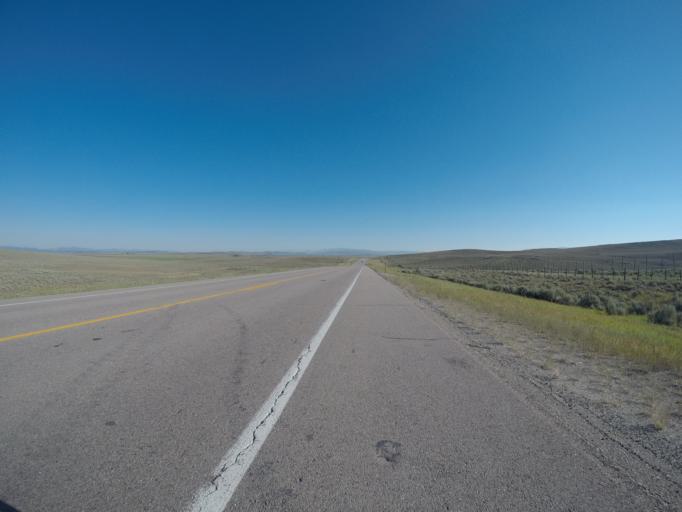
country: US
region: Wyoming
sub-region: Sublette County
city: Pinedale
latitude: 42.9153
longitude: -110.0788
